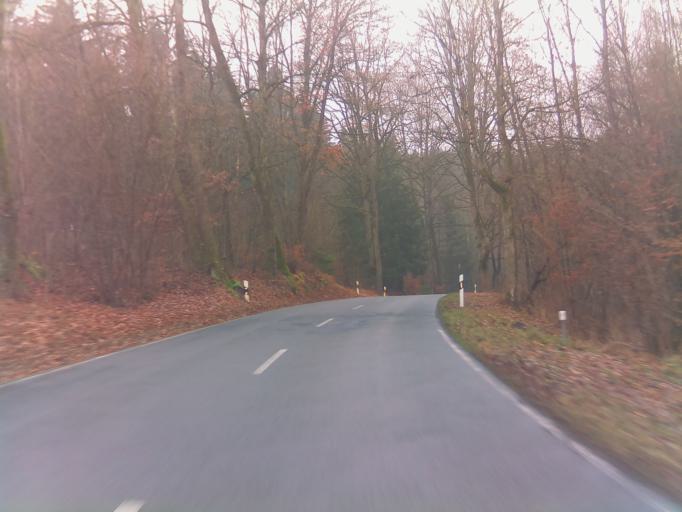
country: DE
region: Thuringia
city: Ehrenberg
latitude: 50.4855
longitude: 10.6887
